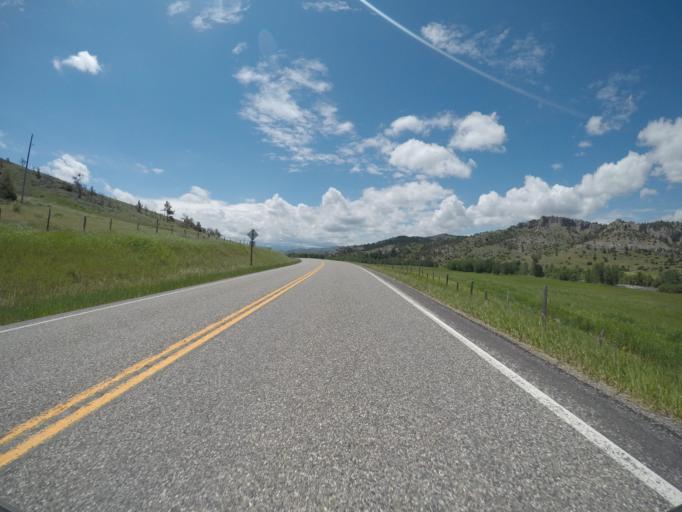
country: US
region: Montana
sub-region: Sweet Grass County
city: Big Timber
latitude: 45.7093
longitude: -110.0080
